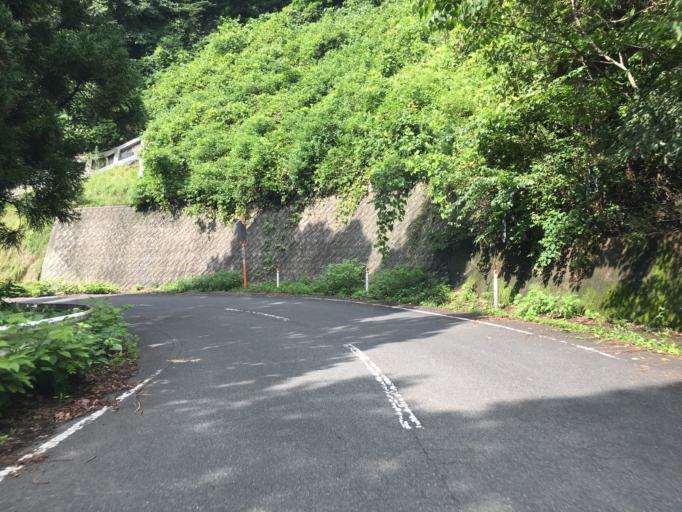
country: JP
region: Miyagi
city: Marumori
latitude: 37.8836
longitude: 140.8564
